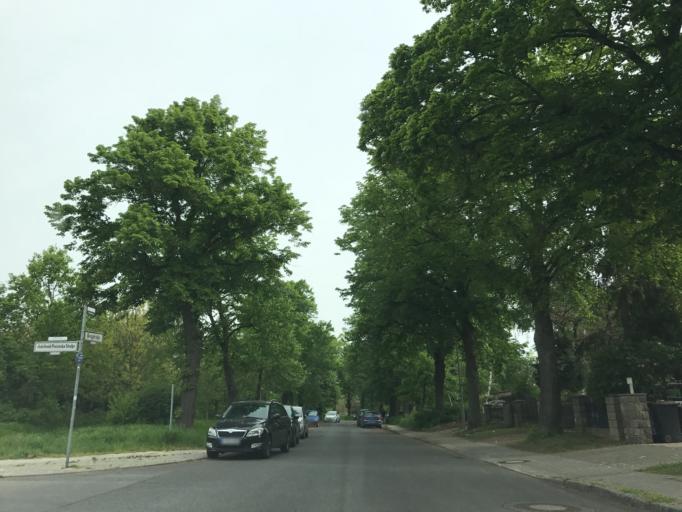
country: DE
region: Berlin
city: Staaken
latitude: 52.5268
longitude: 13.1439
